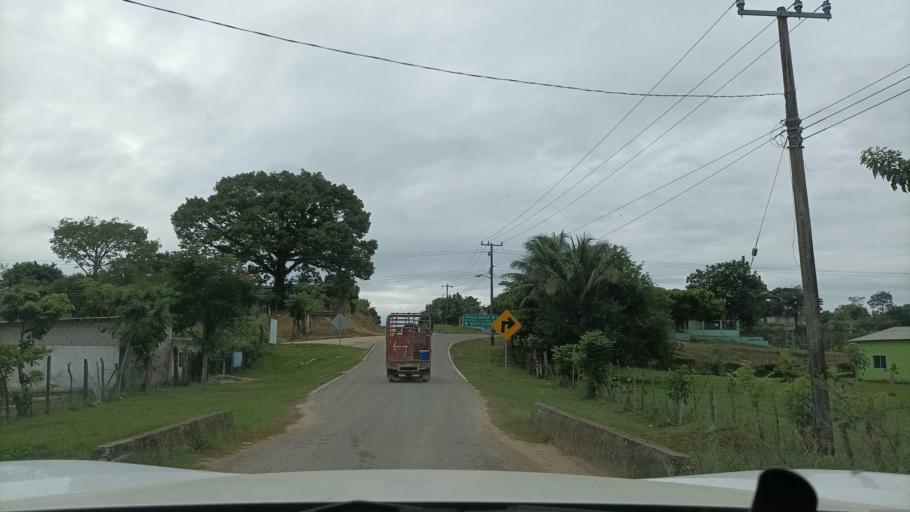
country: MX
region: Veracruz
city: Hidalgotitlan
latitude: 17.6584
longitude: -94.4040
